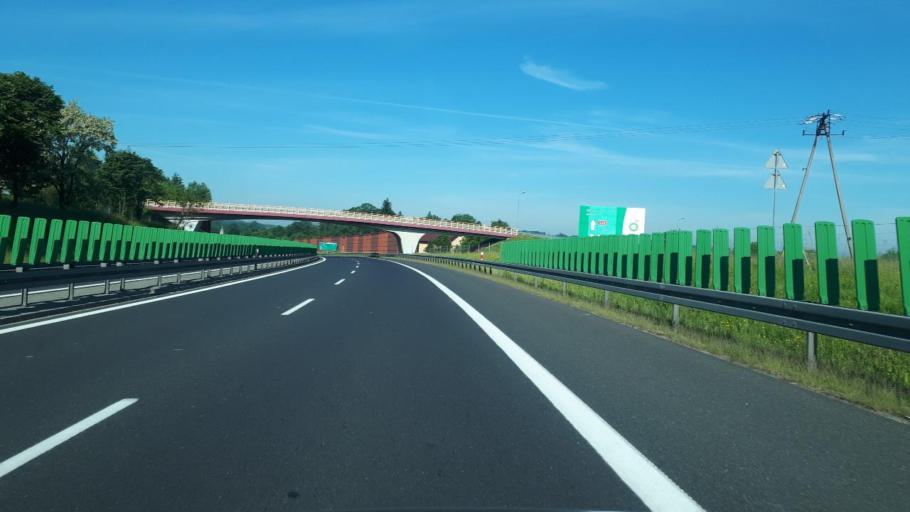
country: PL
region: Silesian Voivodeship
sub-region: Powiat bielski
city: Jasienica
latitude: 49.8161
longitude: 18.9321
